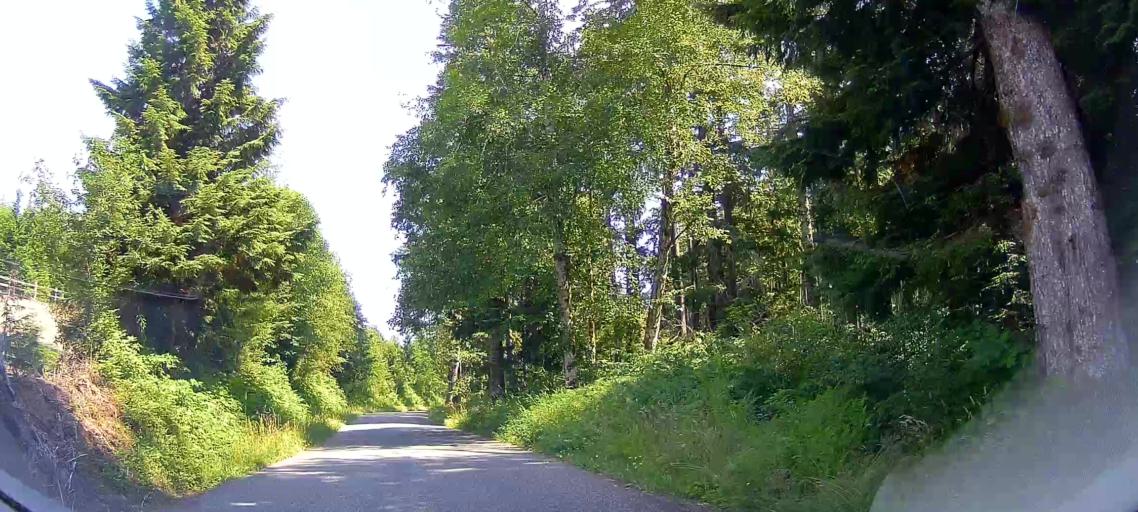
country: US
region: Washington
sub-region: Snohomish County
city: Arlington Heights
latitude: 48.3126
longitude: -121.9783
